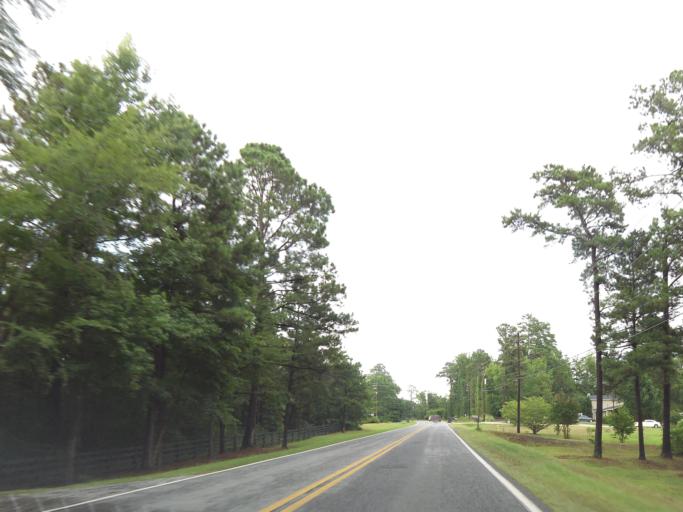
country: US
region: Georgia
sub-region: Bibb County
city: West Point
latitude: 32.8324
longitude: -83.7526
